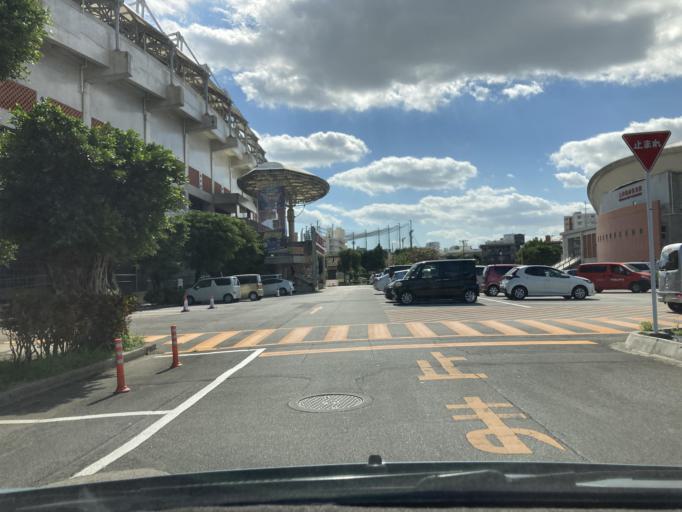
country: JP
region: Okinawa
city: Okinawa
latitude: 26.3334
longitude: 127.7875
